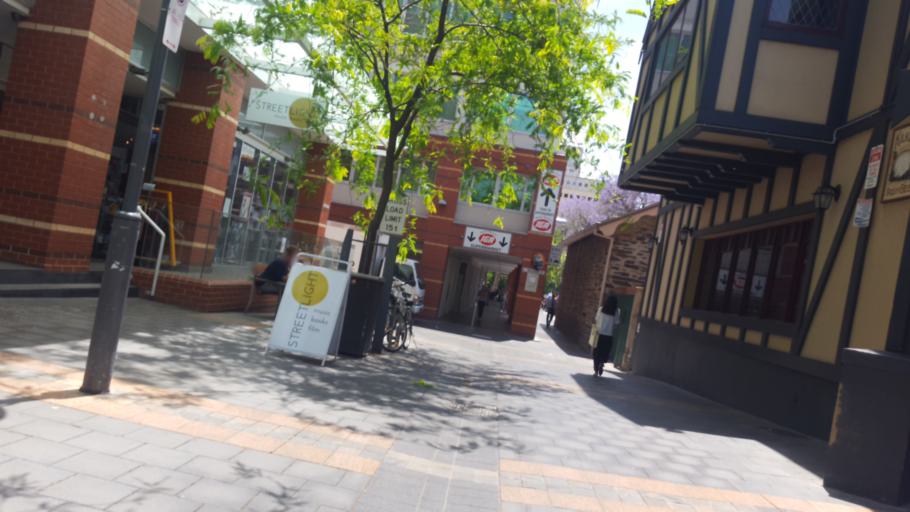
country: AU
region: South Australia
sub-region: Adelaide
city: Adelaide
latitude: -34.9217
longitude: 138.6087
